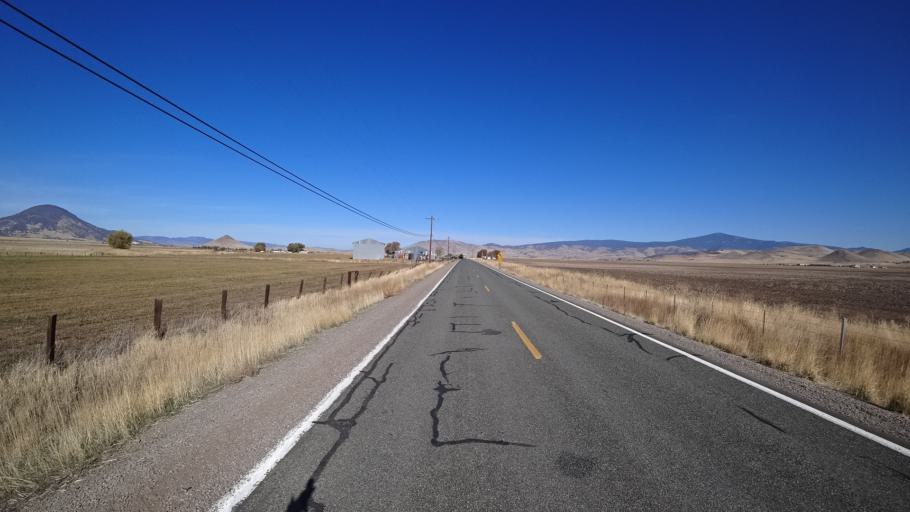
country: US
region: California
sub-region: Siskiyou County
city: Montague
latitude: 41.7751
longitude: -122.4761
